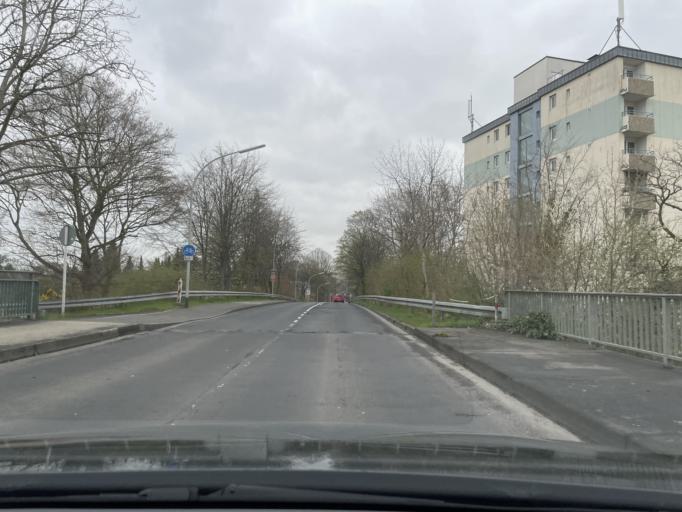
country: DE
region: North Rhine-Westphalia
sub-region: Regierungsbezirk Dusseldorf
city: Monchengladbach
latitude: 51.1243
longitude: 6.4358
